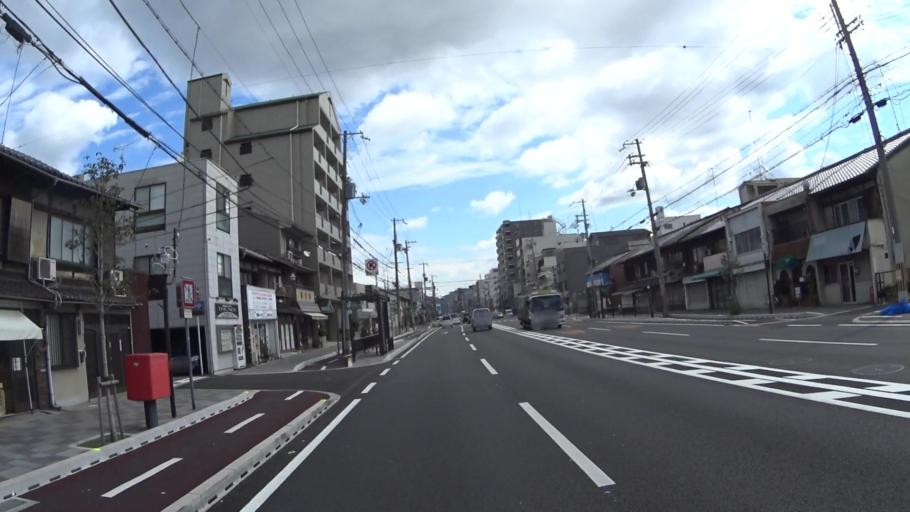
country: JP
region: Kyoto
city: Kyoto
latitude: 34.9892
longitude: 135.7449
